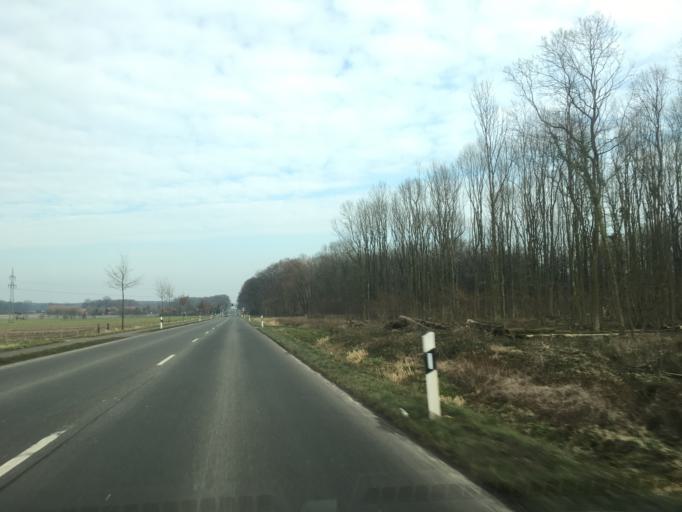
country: DE
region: North Rhine-Westphalia
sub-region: Regierungsbezirk Munster
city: Dulmen
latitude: 51.8484
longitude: 7.3053
